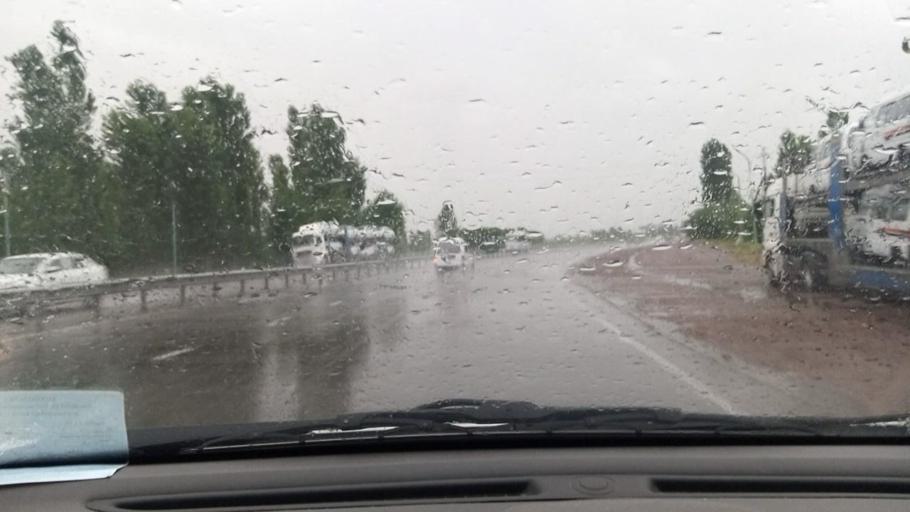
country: UZ
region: Toshkent
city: Ohangaron
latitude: 40.9098
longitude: 69.7498
